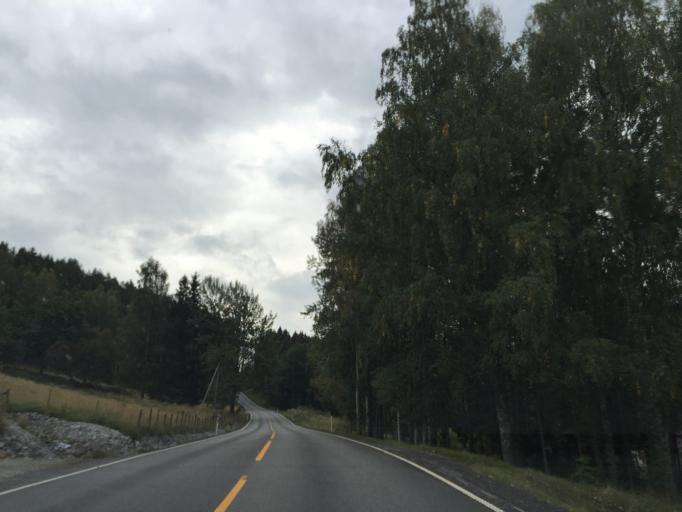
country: NO
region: Hedmark
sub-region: Loten
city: Loten
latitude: 60.6807
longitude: 11.3507
